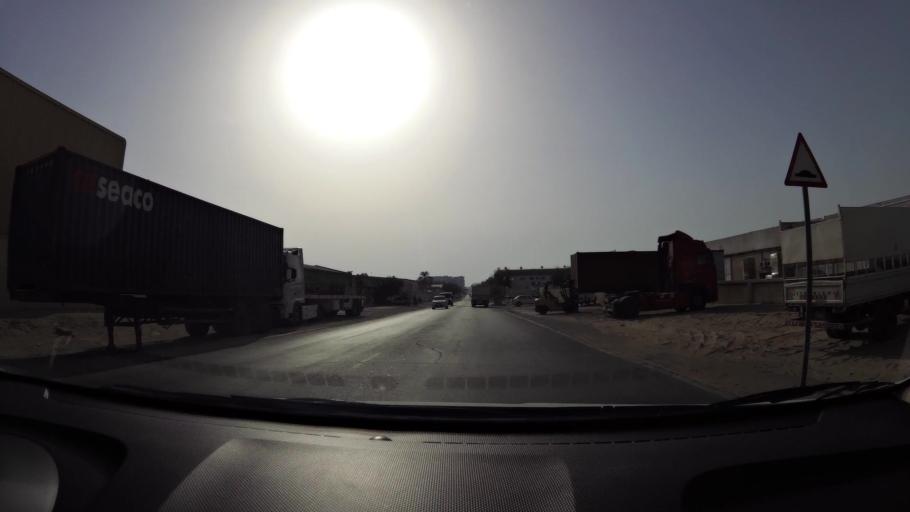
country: AE
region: Ash Shariqah
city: Sharjah
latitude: 25.2288
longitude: 55.3684
